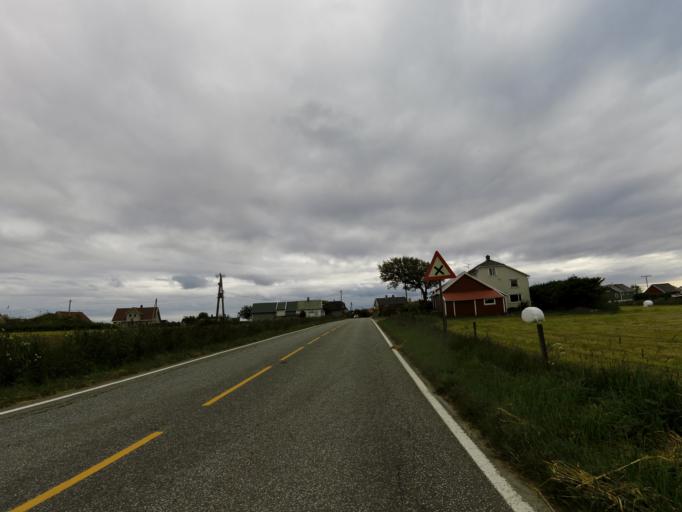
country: NO
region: Vest-Agder
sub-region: Farsund
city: Vestbygd
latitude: 58.1261
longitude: 6.6110
